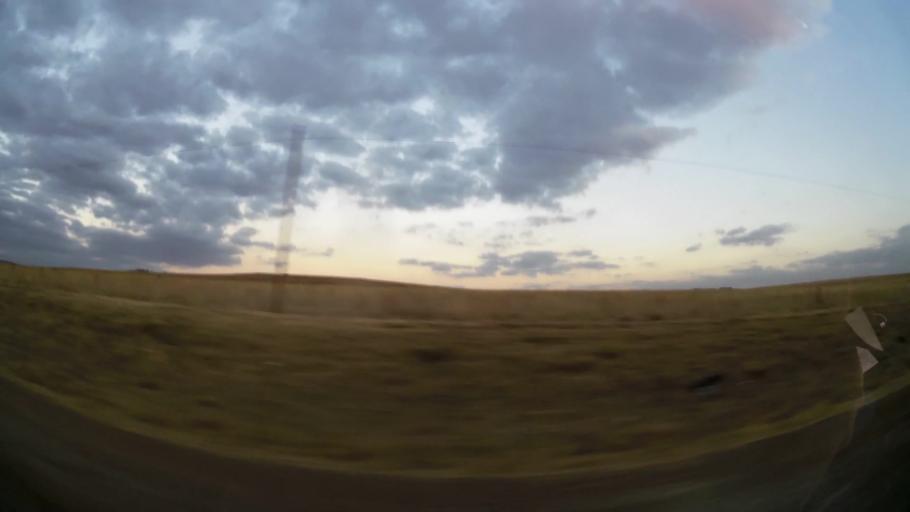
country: ZA
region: Gauteng
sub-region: West Rand District Municipality
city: Krugersdorp
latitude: -26.0518
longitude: 27.7108
